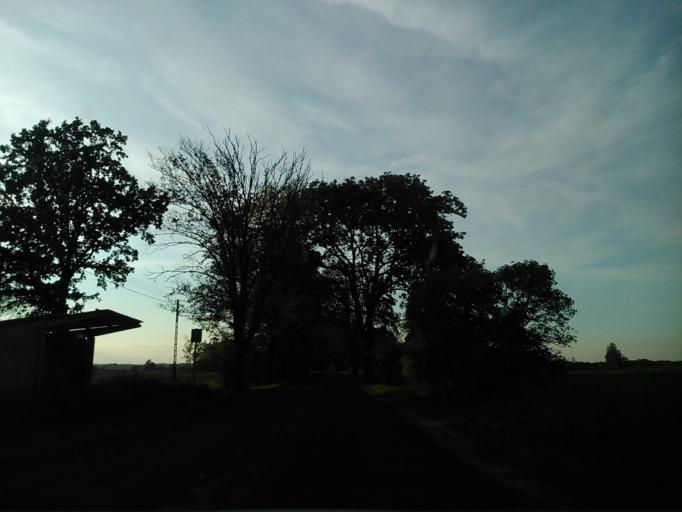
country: PL
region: Kujawsko-Pomorskie
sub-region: Powiat wabrzeski
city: Debowa Laka
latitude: 53.2455
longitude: 19.1312
